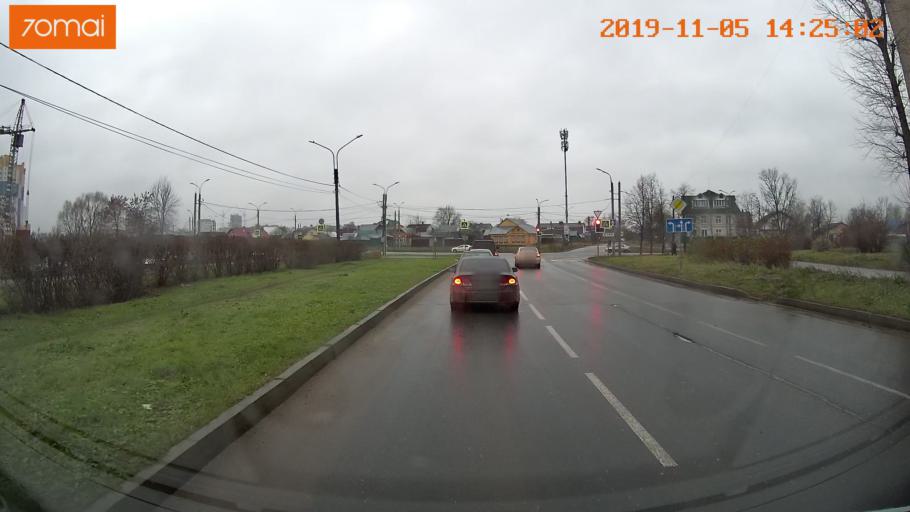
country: RU
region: Ivanovo
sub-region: Gorod Ivanovo
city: Ivanovo
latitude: 56.9708
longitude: 40.9939
